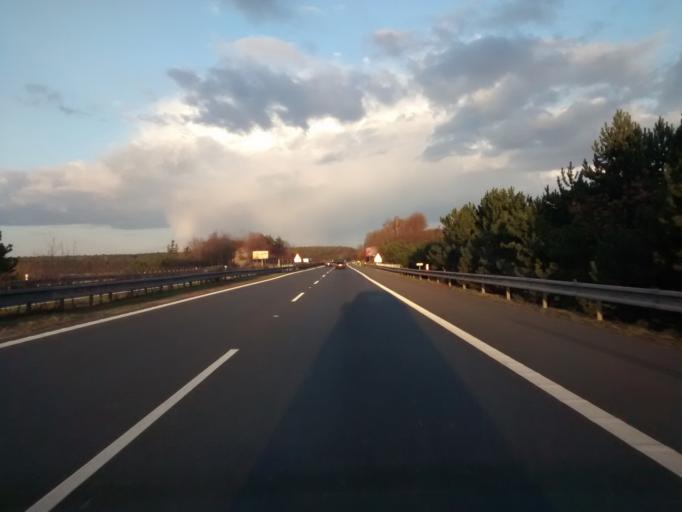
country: CZ
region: Central Bohemia
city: Poricany
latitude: 50.1284
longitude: 14.8909
